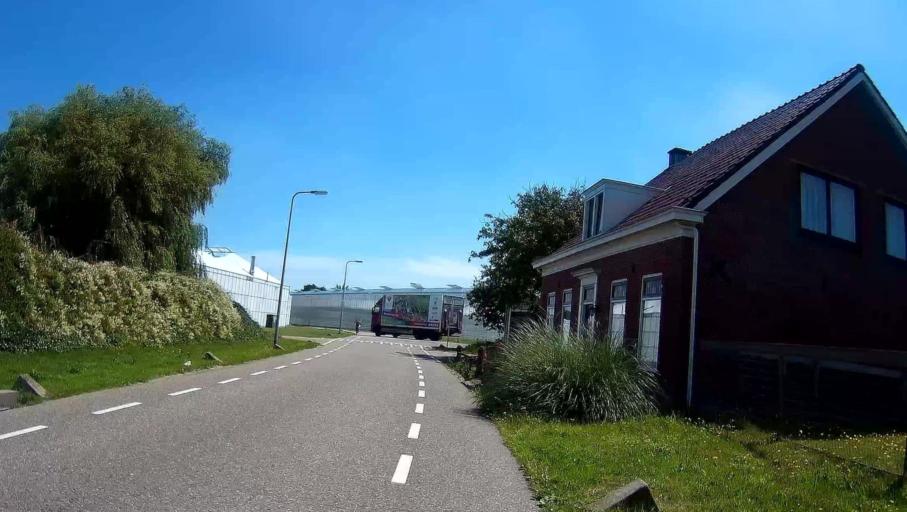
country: NL
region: South Holland
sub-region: Gemeente Westland
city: Monster
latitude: 52.0138
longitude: 4.1800
